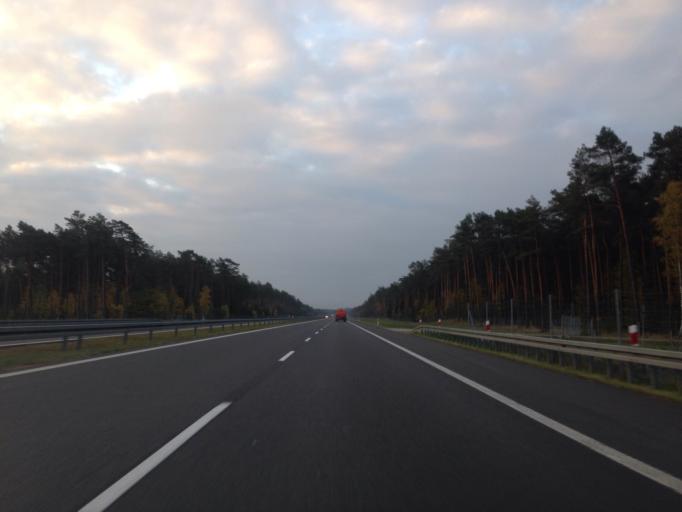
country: PL
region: Kujawsko-Pomorskie
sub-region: Powiat swiecki
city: Warlubie
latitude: 53.5193
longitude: 18.6022
